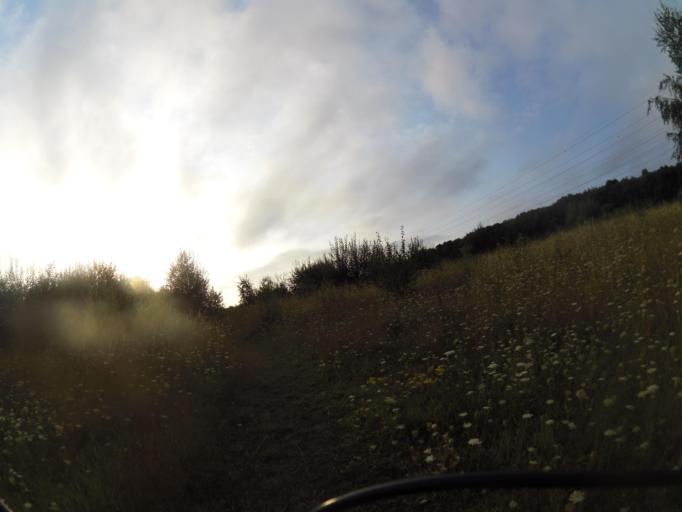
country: GB
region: England
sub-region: Suffolk
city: Bramford
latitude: 52.0343
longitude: 1.1086
